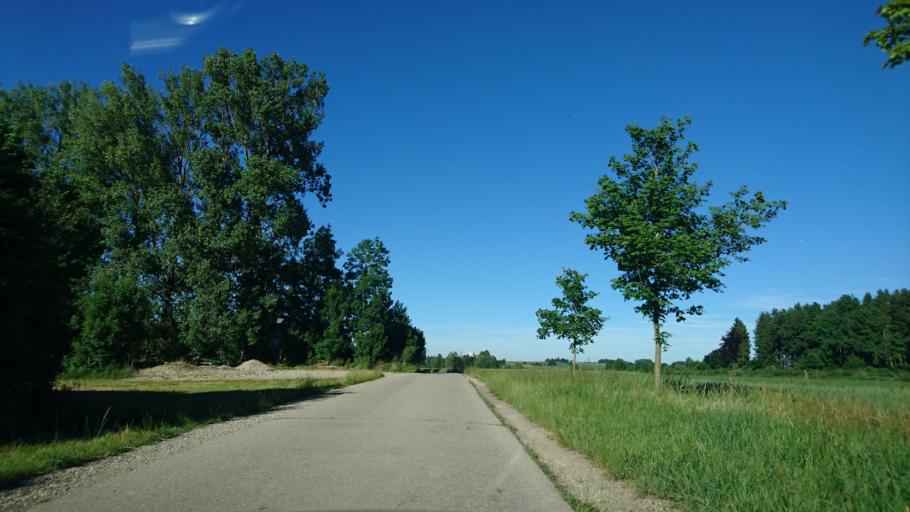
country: DE
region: Bavaria
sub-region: Upper Bavaria
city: Poing
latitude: 48.1786
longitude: 11.8358
